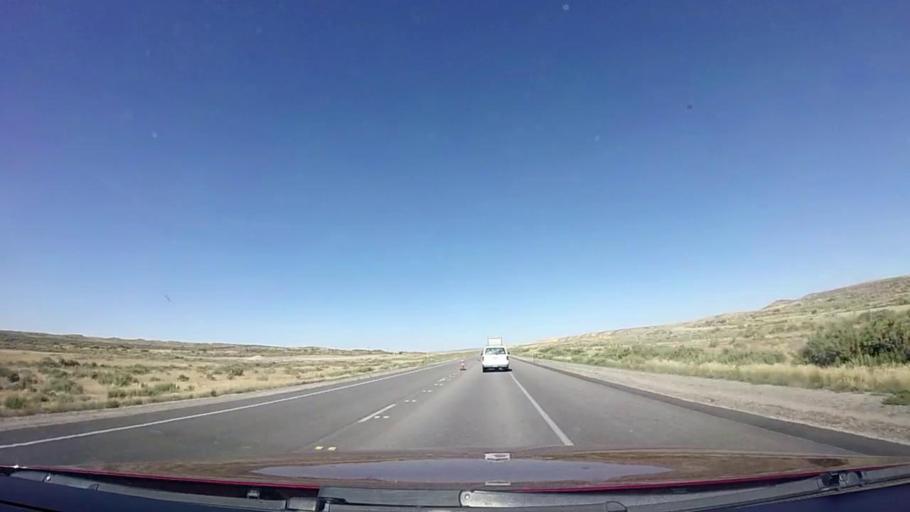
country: US
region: Wyoming
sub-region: Carbon County
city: Rawlins
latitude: 41.7062
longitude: -107.8581
